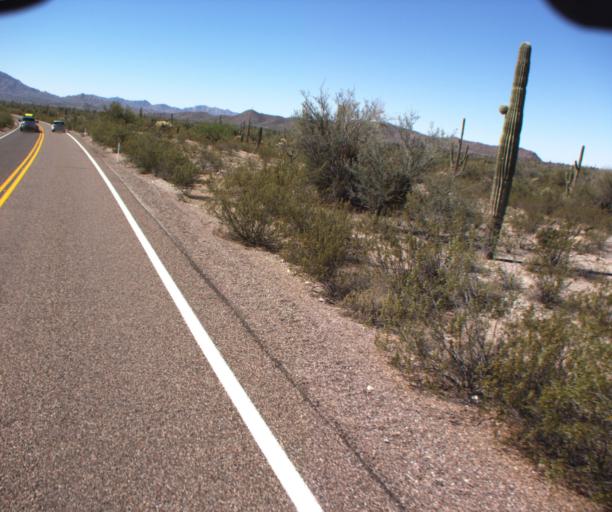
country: MX
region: Sonora
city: Sonoyta
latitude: 31.9115
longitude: -112.8092
